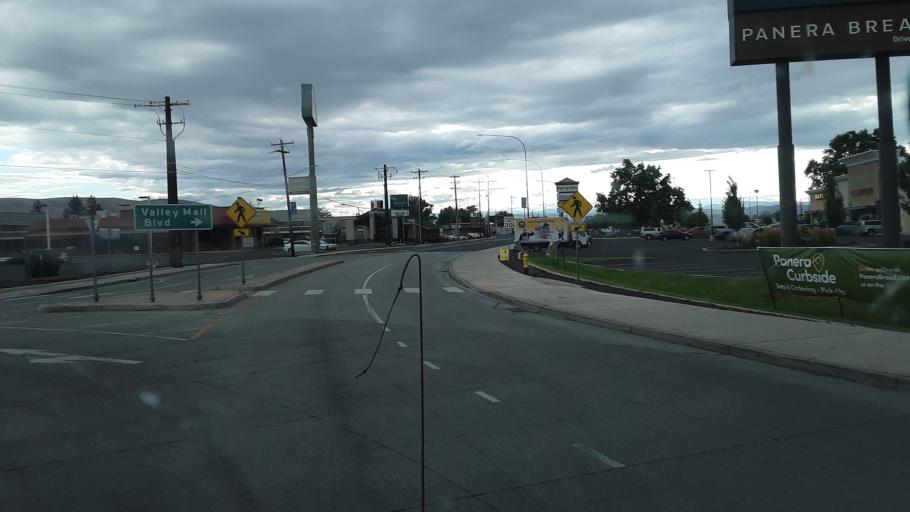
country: US
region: Washington
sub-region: Yakima County
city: Union Gap
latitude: 46.5632
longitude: -120.4752
